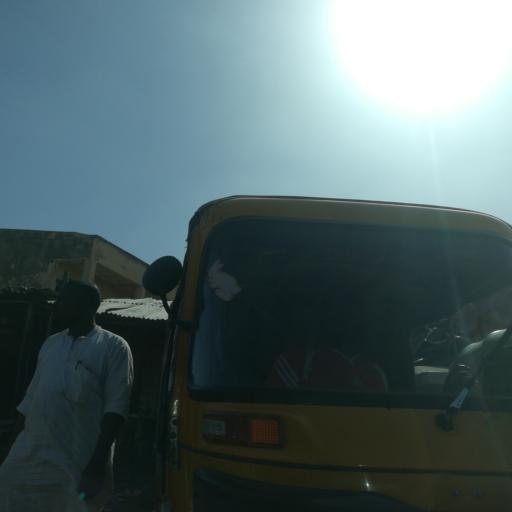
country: NG
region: Kano
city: Kano
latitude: 12.0049
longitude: 8.5238
